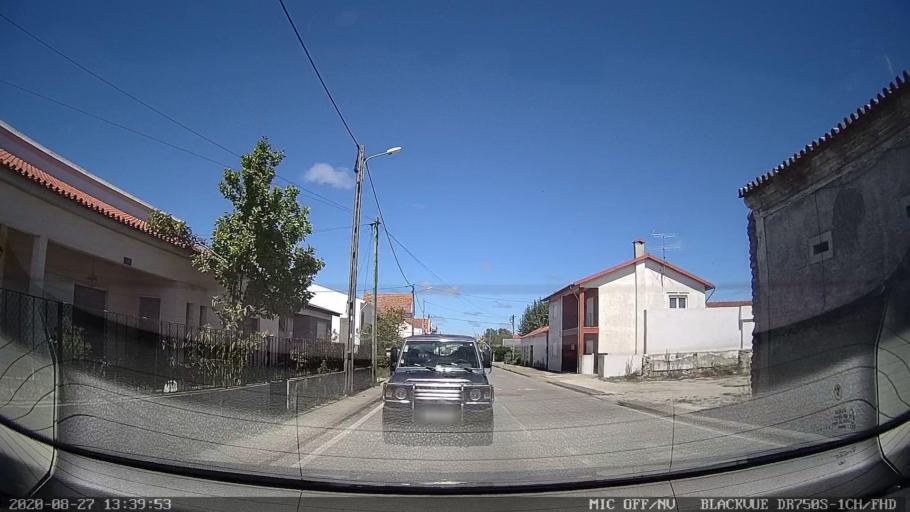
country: PT
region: Coimbra
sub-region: Mira
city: Mira
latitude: 40.4379
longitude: -8.7282
